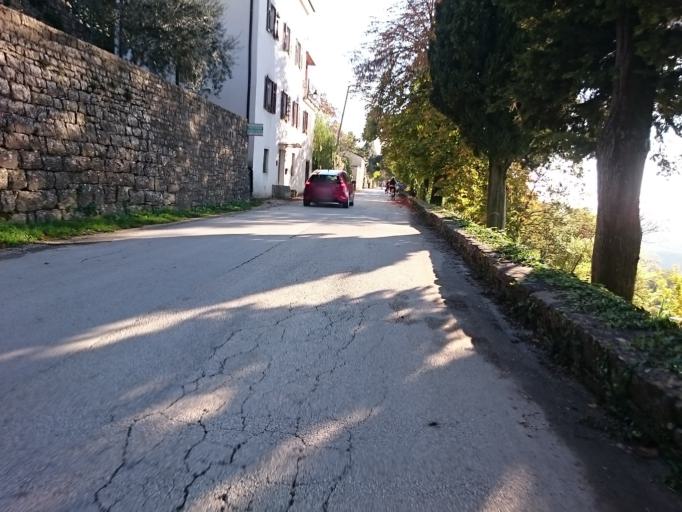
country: HR
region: Istarska
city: Buje
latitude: 45.3816
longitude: 13.7232
